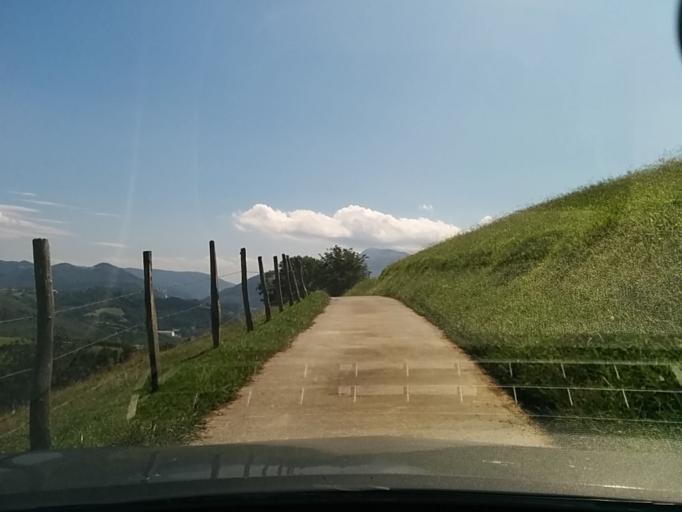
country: ES
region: Basque Country
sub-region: Provincia de Guipuzcoa
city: Zumaia
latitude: 43.2886
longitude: -2.2736
